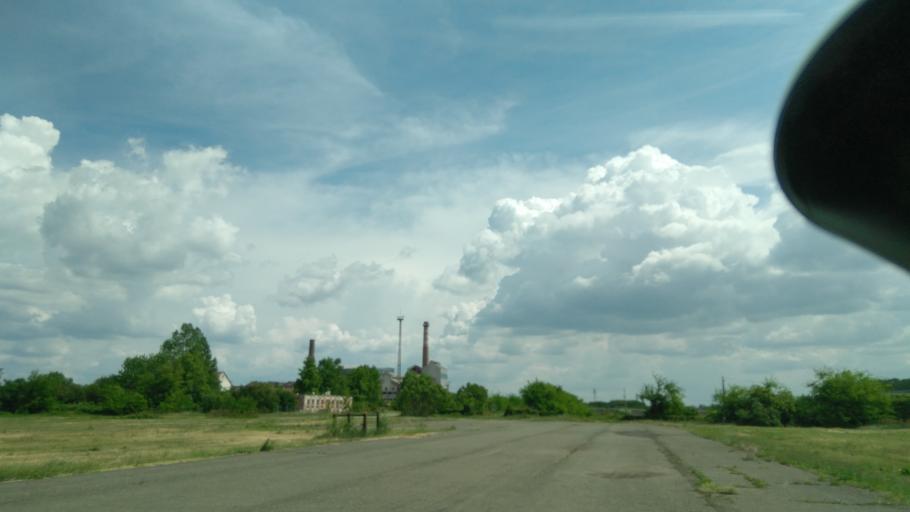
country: HU
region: Bekes
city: Mezohegyes
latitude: 46.3126
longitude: 20.8056
